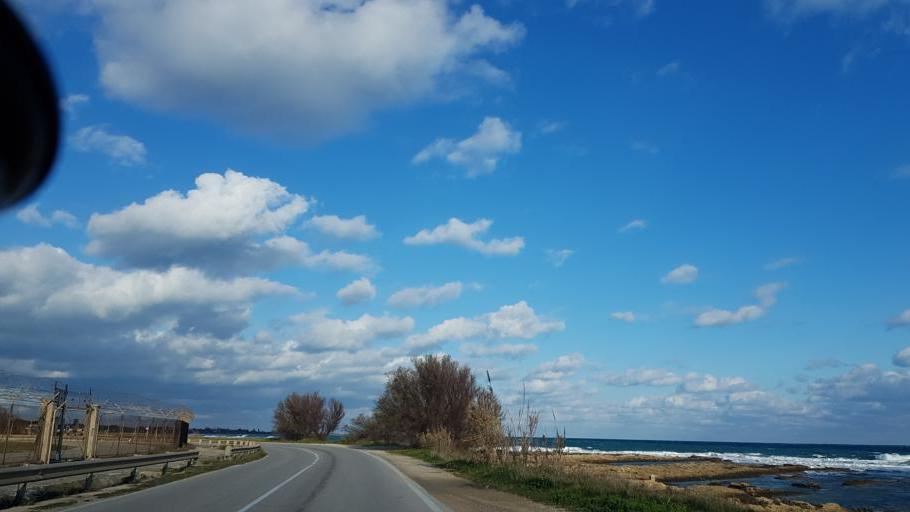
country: IT
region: Apulia
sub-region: Provincia di Brindisi
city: Materdomini
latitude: 40.6631
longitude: 17.9571
